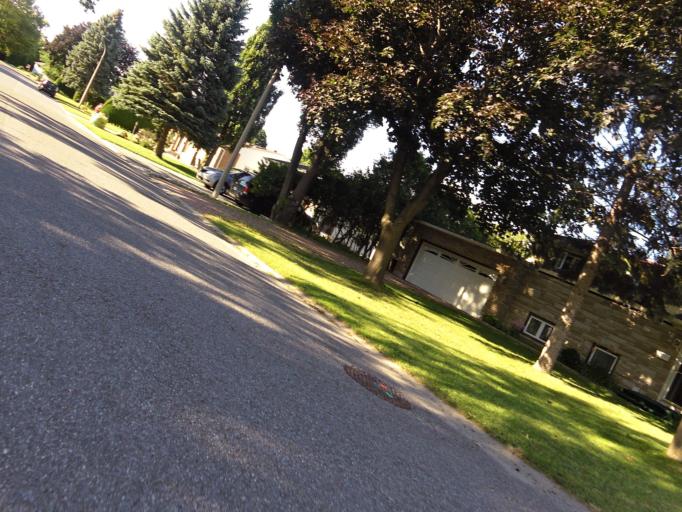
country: CA
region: Ontario
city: Ottawa
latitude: 45.3460
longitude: -75.7211
